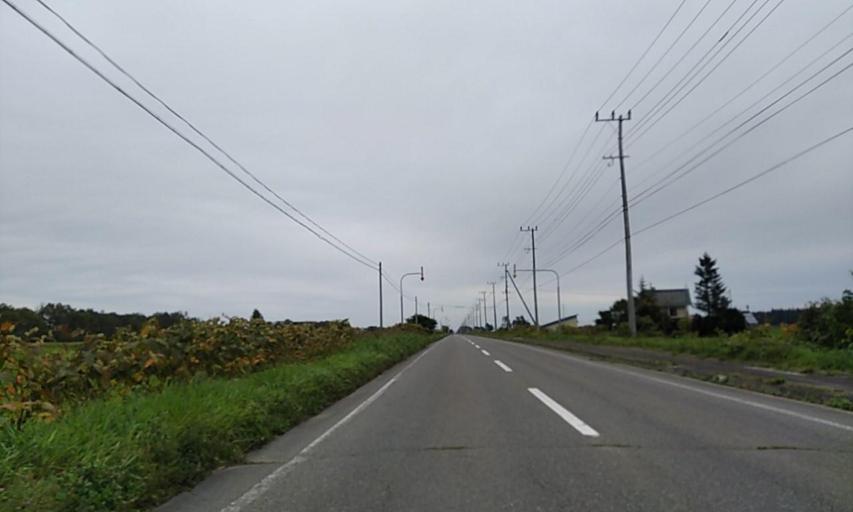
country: JP
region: Hokkaido
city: Obihiro
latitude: 42.6543
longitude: 143.1035
